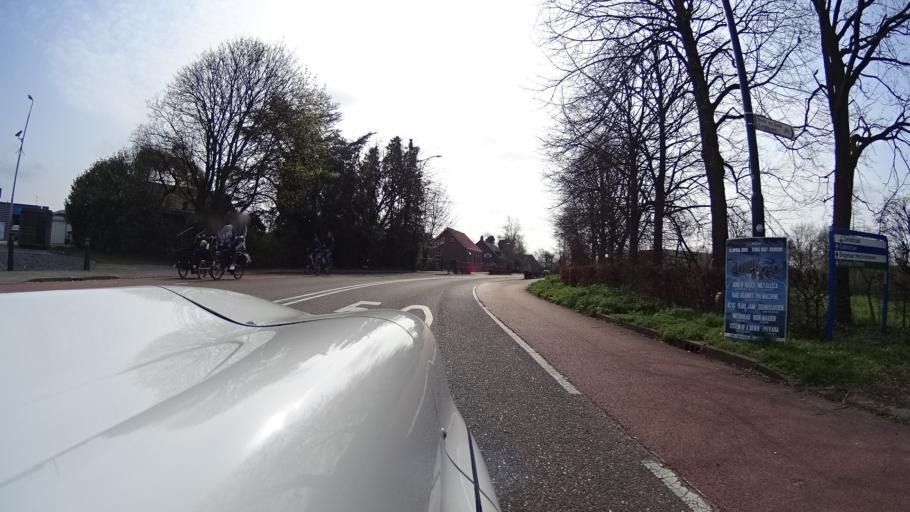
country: NL
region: North Brabant
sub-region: Gemeente Boekel
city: Boekel
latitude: 51.5458
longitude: 5.6899
